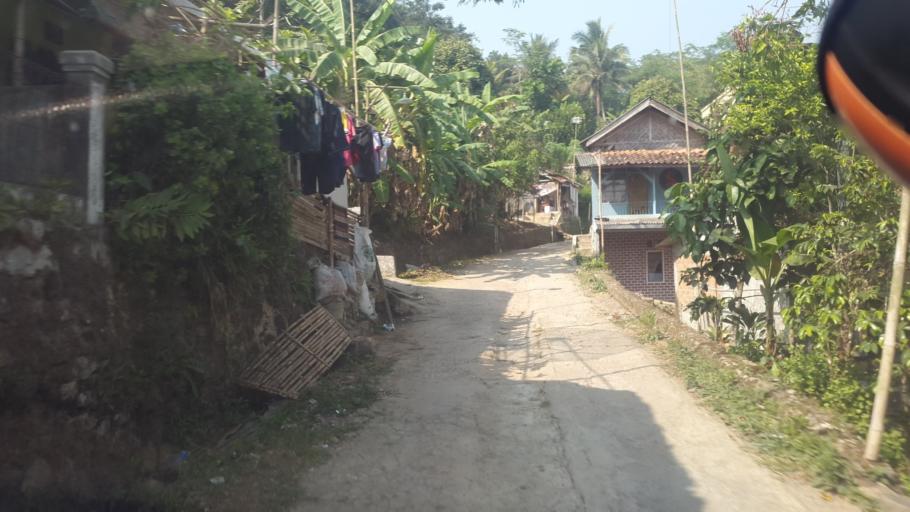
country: ID
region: West Java
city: Gunungkalong
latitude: -6.8974
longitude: 106.7989
